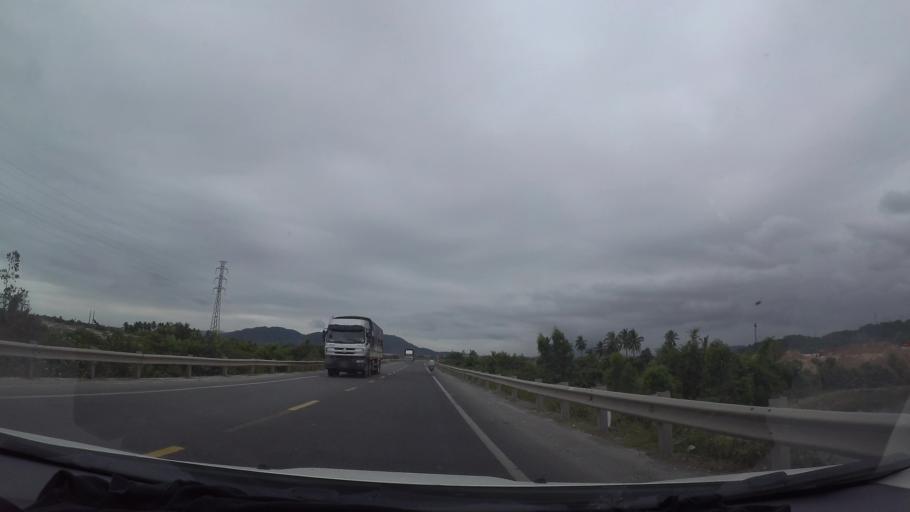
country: VN
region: Da Nang
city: Lien Chieu
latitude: 16.1122
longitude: 108.1049
